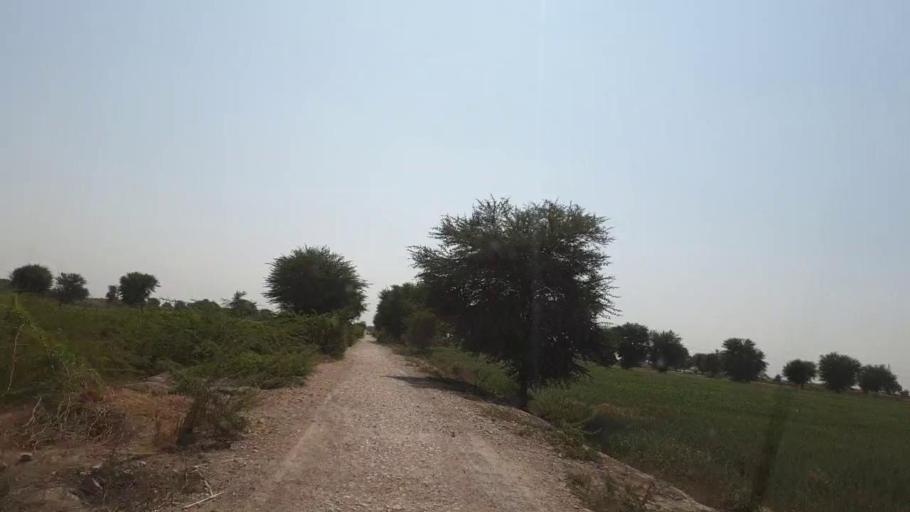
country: PK
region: Sindh
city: Kunri
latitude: 25.0785
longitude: 69.5339
